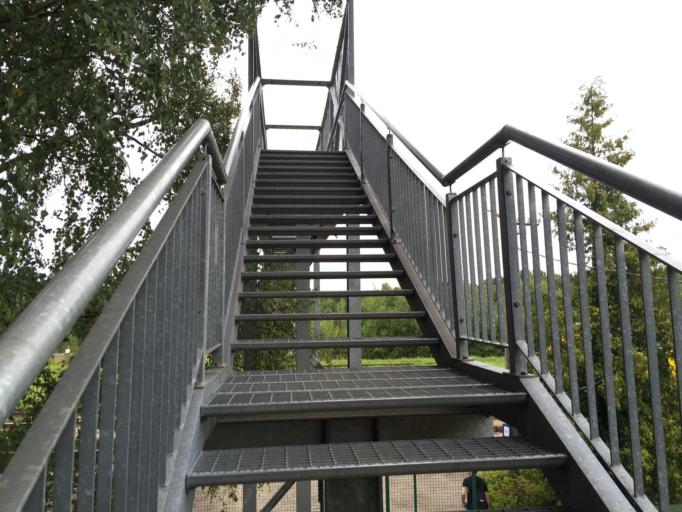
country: LV
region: Zilupes
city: Zilupe
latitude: 56.3915
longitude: 28.1164
